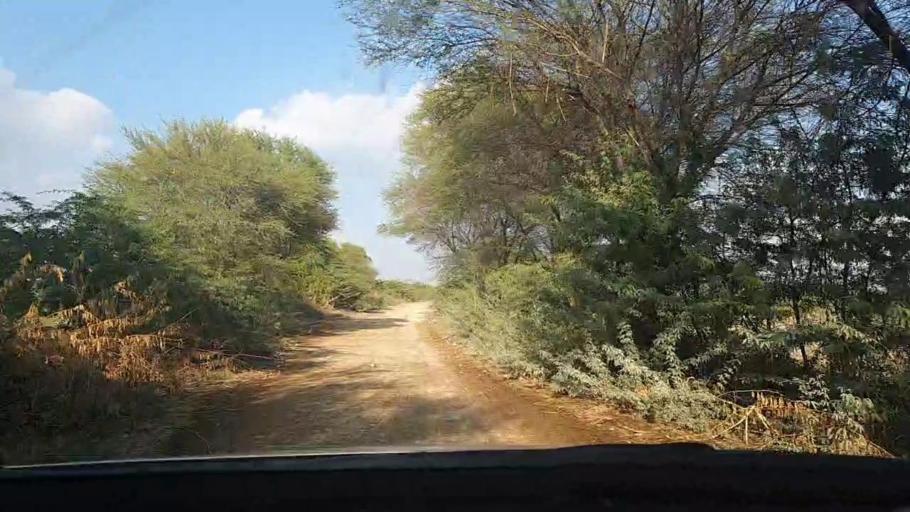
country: PK
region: Sindh
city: Tando Mittha Khan
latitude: 25.8958
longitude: 69.2993
